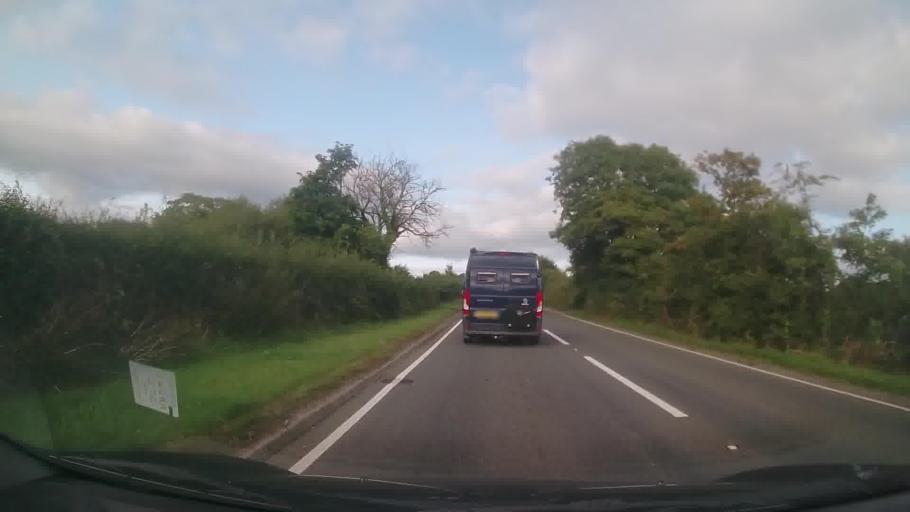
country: GB
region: Wales
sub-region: Pembrokeshire
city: Jeffreyston
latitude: 51.7158
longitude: -4.7587
